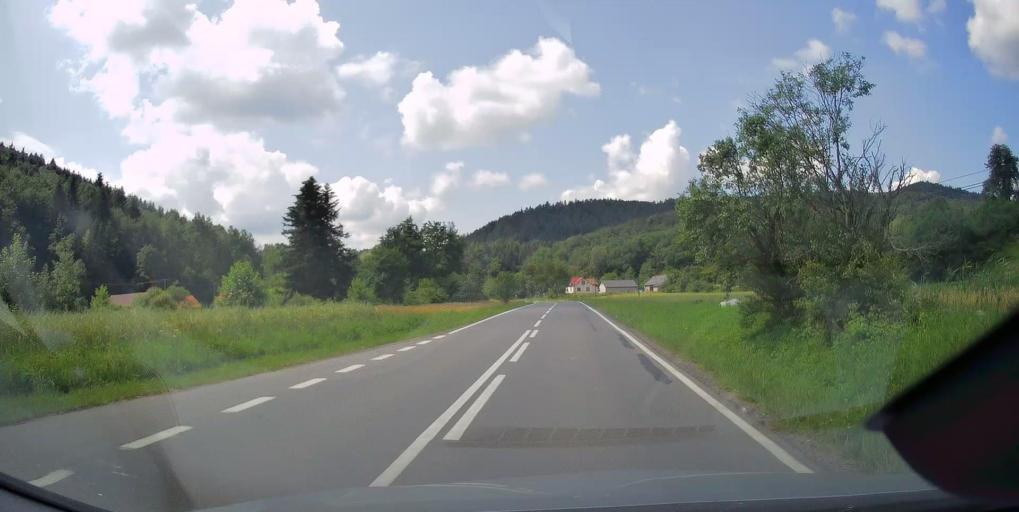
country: PL
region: Lesser Poland Voivodeship
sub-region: Powiat tarnowski
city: Zakliczyn
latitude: 49.8226
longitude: 20.8029
